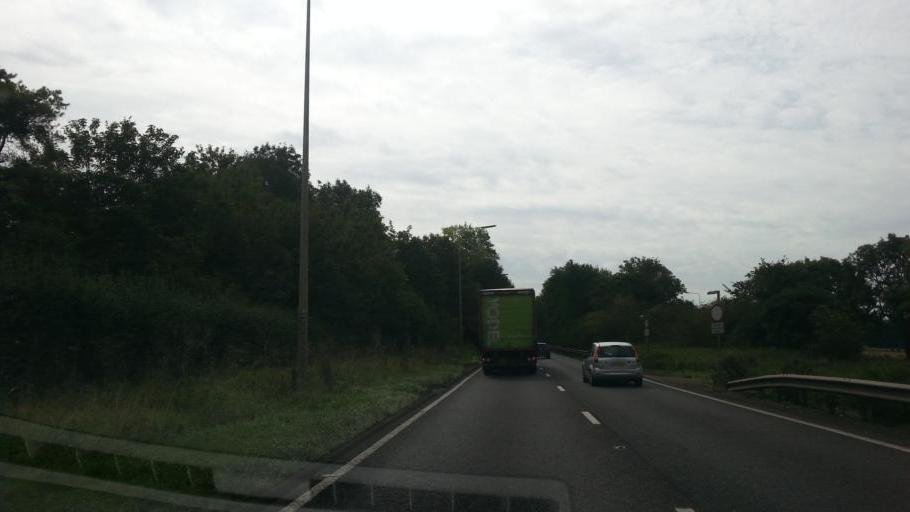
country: GB
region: England
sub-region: Central Bedfordshire
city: Edworth
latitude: 52.0594
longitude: -0.2344
